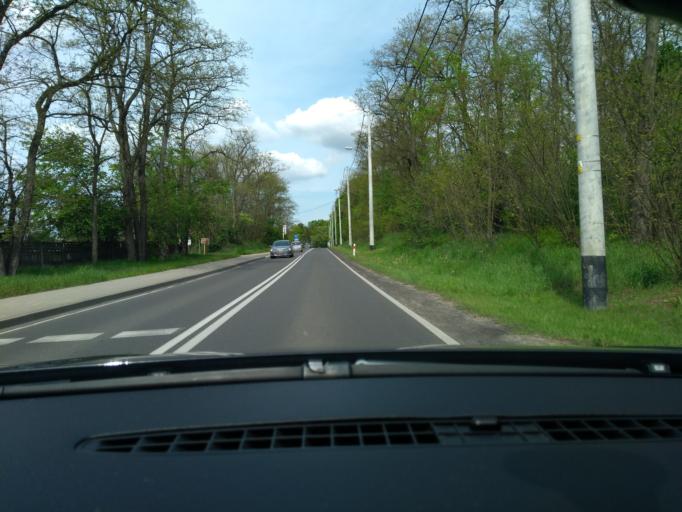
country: PL
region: West Pomeranian Voivodeship
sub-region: Powiat gryfinski
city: Gryfino
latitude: 53.2710
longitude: 14.5078
